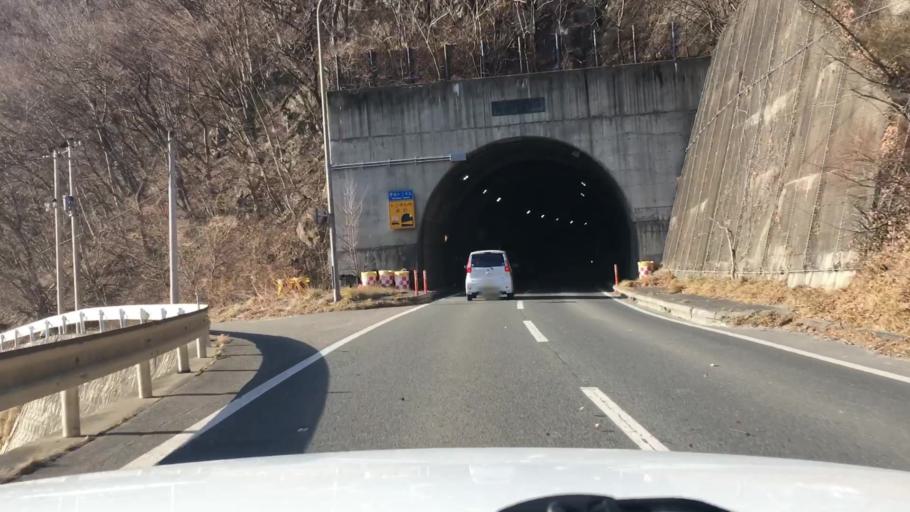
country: JP
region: Iwate
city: Miyako
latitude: 39.5971
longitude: 141.7155
